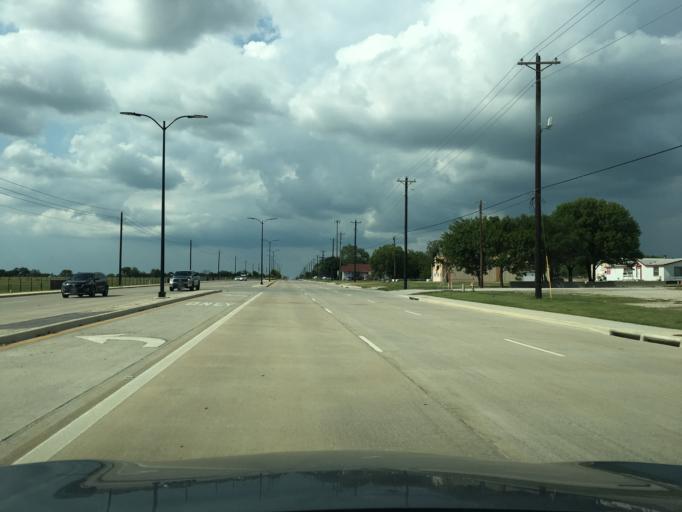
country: US
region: Texas
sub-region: Denton County
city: Oak Point
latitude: 33.1703
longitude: -96.9770
